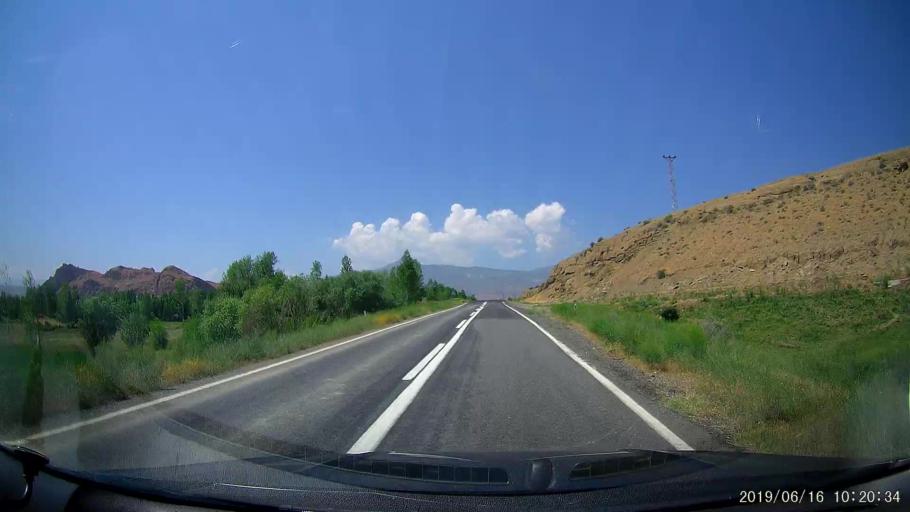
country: TR
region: Igdir
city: Tuzluca
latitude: 40.1466
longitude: 43.6465
